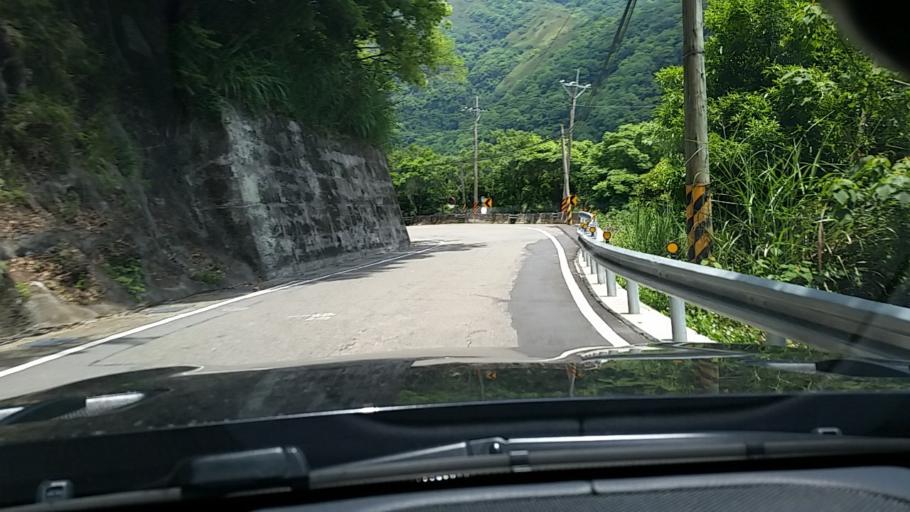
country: TW
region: Taiwan
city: Daxi
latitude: 24.7032
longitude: 121.3640
